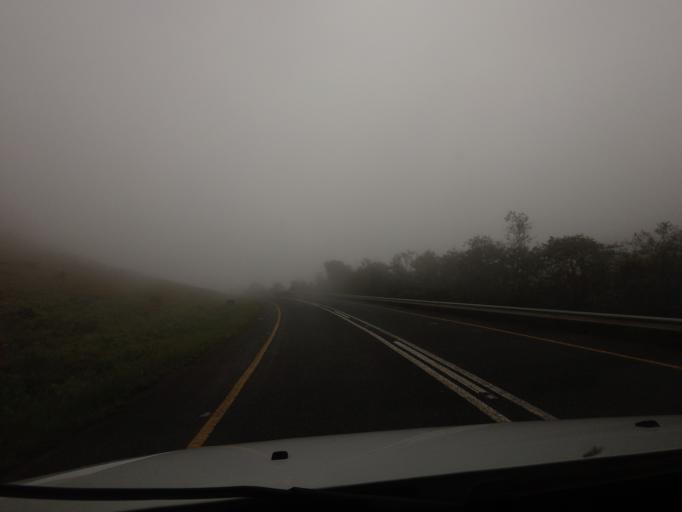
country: ZA
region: Mpumalanga
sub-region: Ehlanzeni District
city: Lydenburg
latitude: -25.1651
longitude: 30.6375
